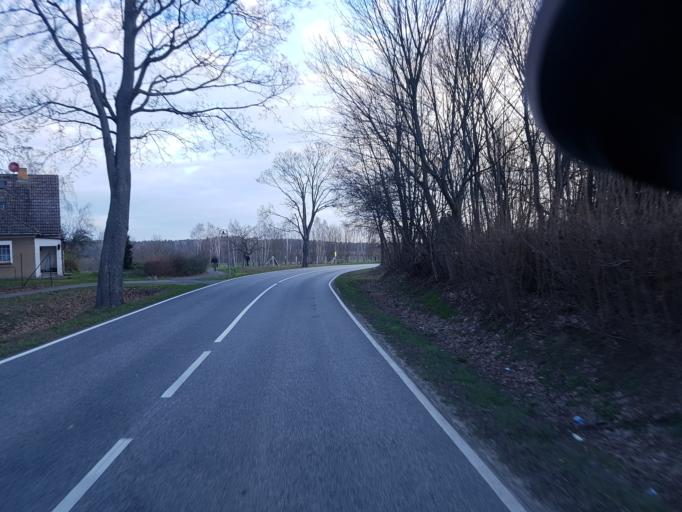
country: DE
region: Brandenburg
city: Drahnsdorf
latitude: 51.8183
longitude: 13.6021
